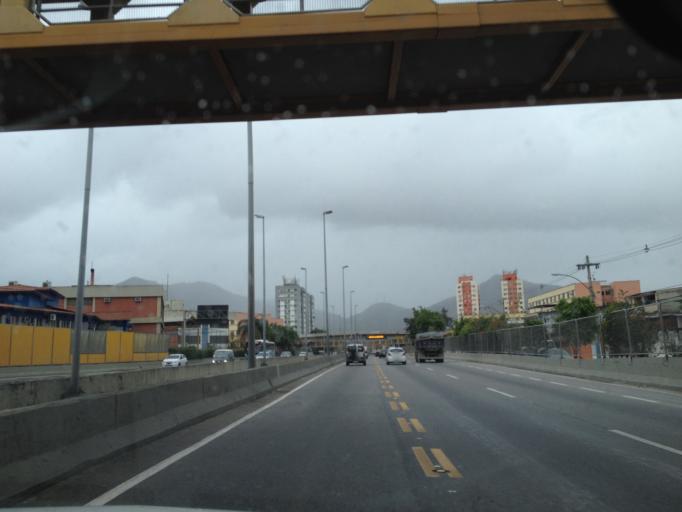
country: BR
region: Rio de Janeiro
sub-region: Rio De Janeiro
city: Rio de Janeiro
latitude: -22.8873
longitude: -43.2931
